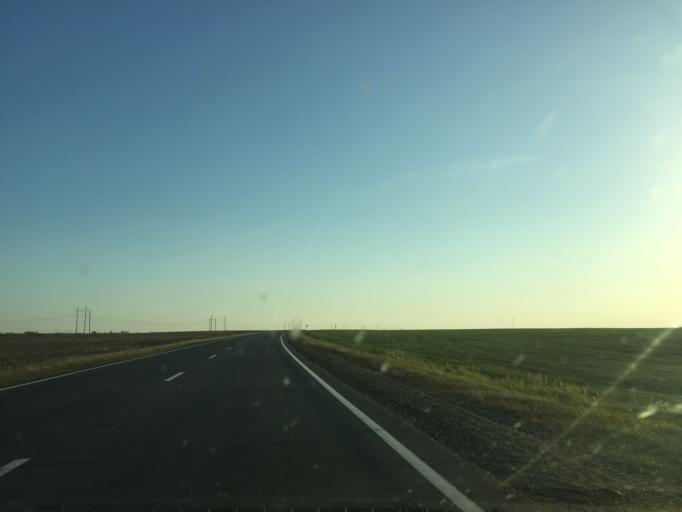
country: BY
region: Mogilev
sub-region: Mahilyowski Rayon
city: Kadino
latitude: 53.8358
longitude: 30.4795
